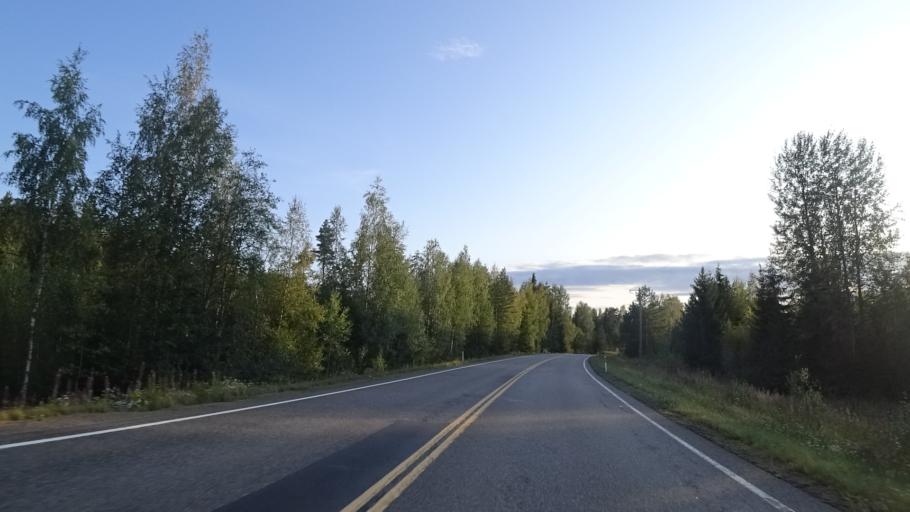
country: FI
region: South Karelia
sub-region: Lappeenranta
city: Ylaemaa
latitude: 60.7264
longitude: 27.9945
